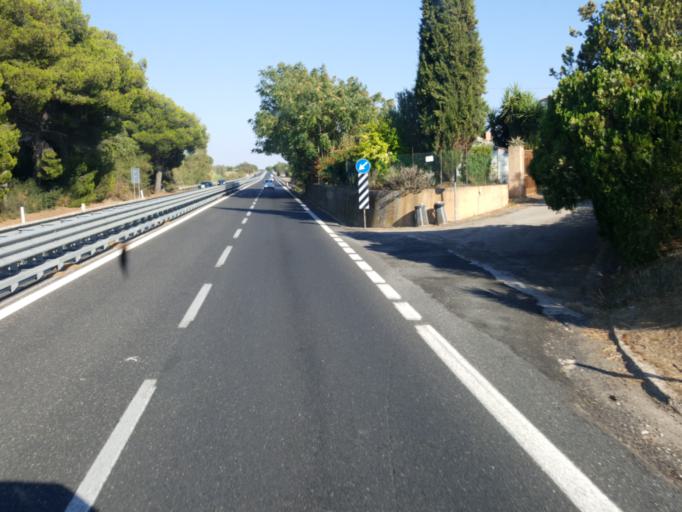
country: IT
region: Latium
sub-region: Provincia di Viterbo
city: Pescia Romana
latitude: 42.3944
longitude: 11.5274
